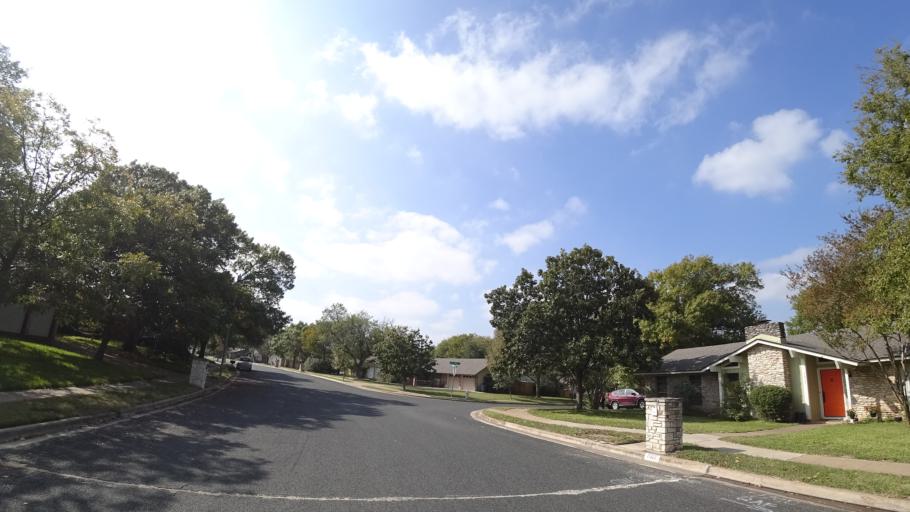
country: US
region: Texas
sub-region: Travis County
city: Shady Hollow
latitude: 30.2043
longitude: -97.8122
